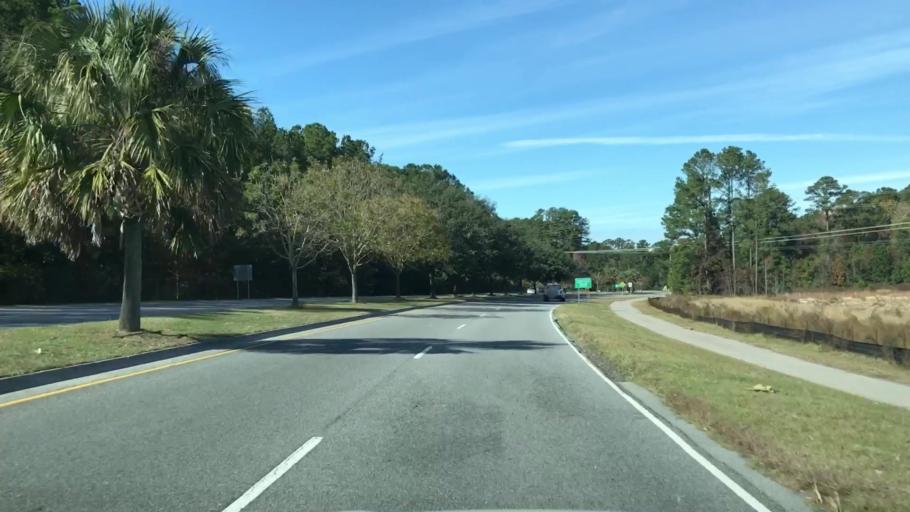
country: US
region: South Carolina
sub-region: Beaufort County
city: Bluffton
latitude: 32.2659
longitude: -80.9122
